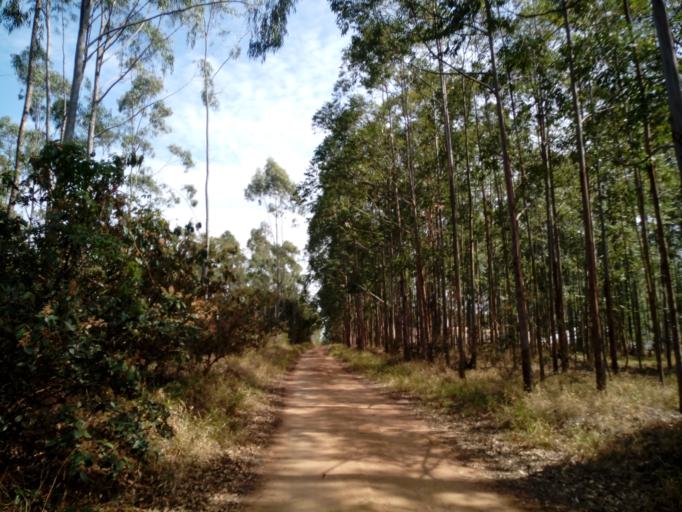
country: BR
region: Sao Paulo
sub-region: Sao Carlos
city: Sao Carlos
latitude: -21.9724
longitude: -47.8772
